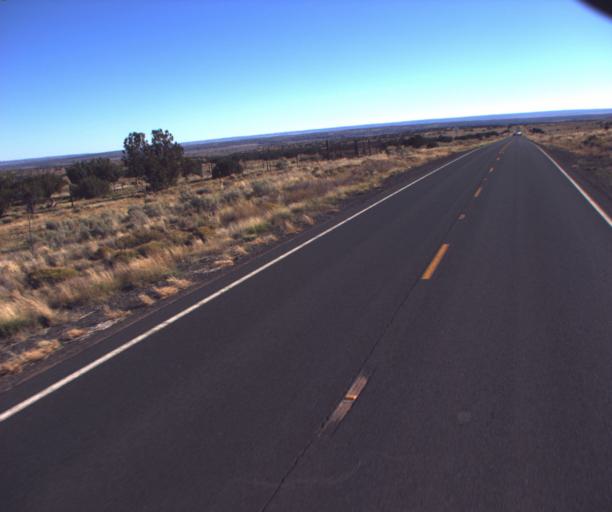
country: US
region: Arizona
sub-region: Apache County
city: Houck
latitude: 35.2557
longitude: -109.4382
